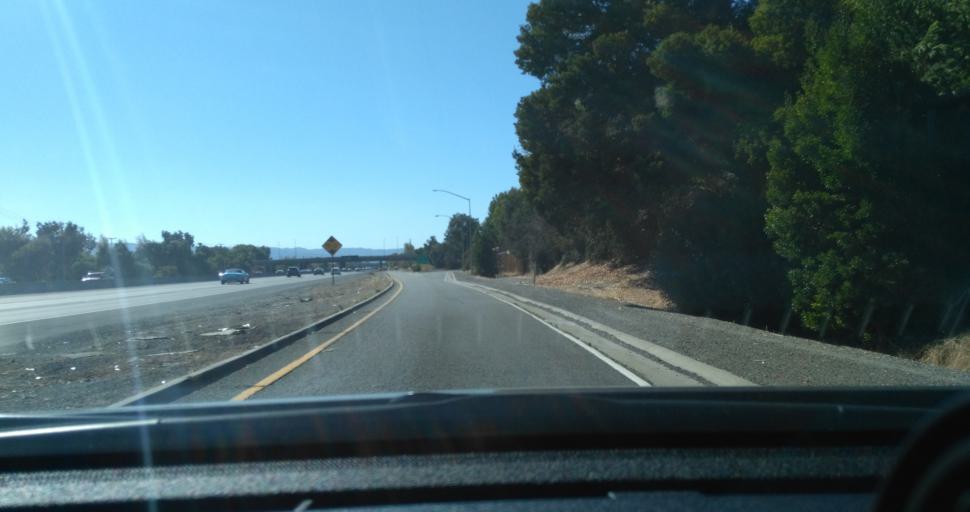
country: US
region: California
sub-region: Santa Clara County
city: Sunnyvale
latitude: 37.4104
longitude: -121.9944
